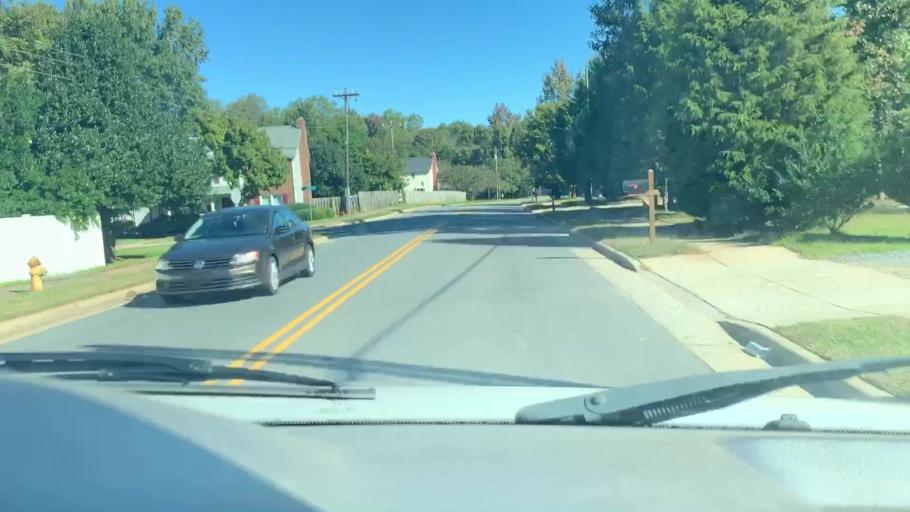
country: US
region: North Carolina
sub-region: Mecklenburg County
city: Charlotte
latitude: 35.2924
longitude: -80.7836
